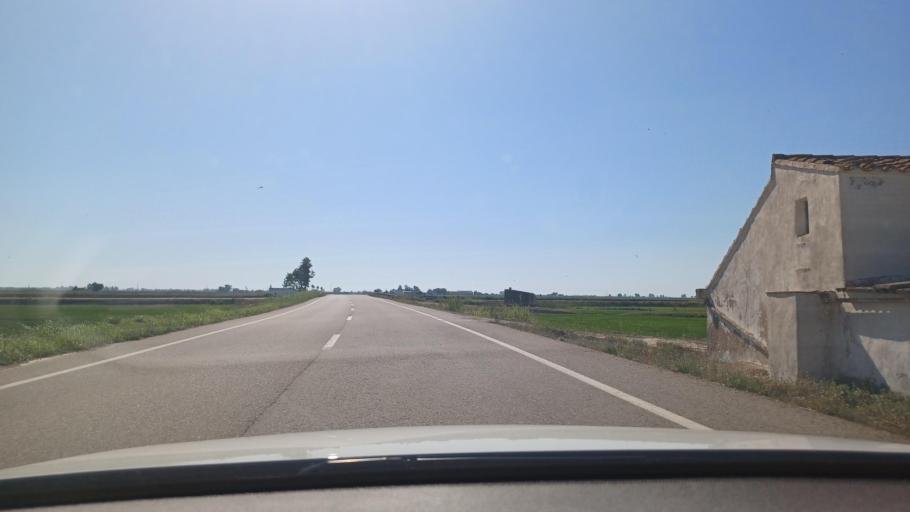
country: ES
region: Catalonia
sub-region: Provincia de Tarragona
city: Deltebre
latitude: 40.7031
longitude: 0.6609
